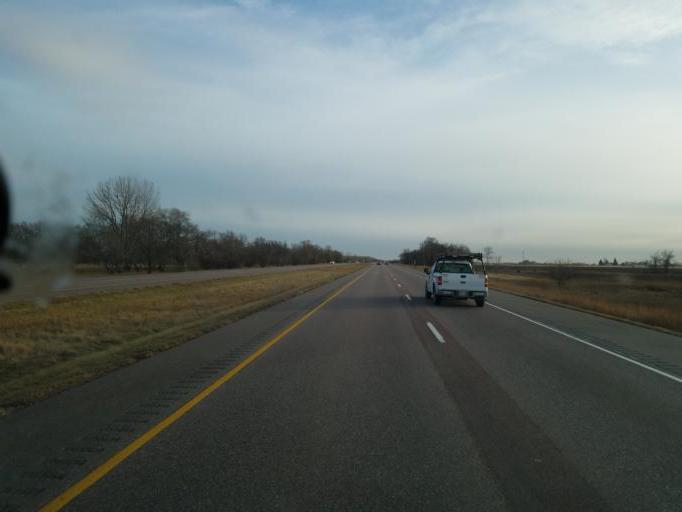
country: US
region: Nebraska
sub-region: Thurston County
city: Macy
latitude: 42.1517
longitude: -96.2201
